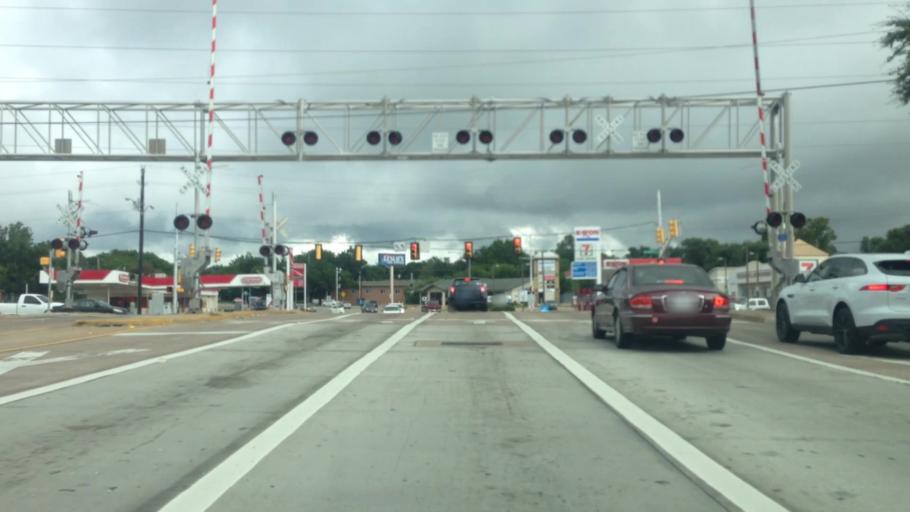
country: US
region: Texas
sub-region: Tarrant County
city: Edgecliff Village
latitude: 32.6598
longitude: -97.4003
